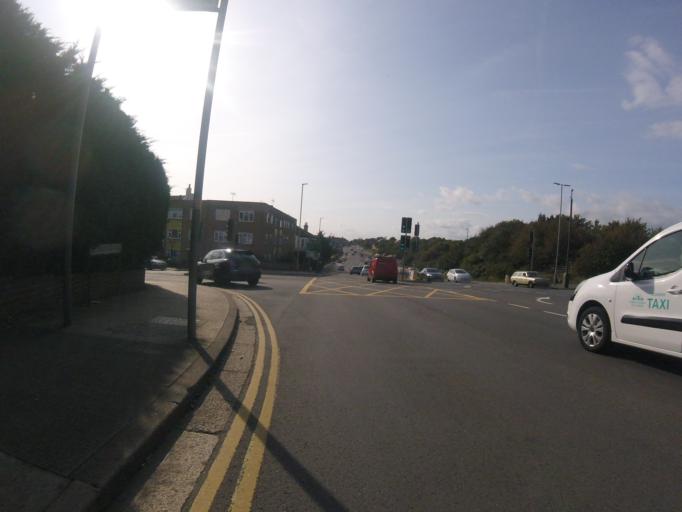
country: GB
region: England
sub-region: East Sussex
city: Portslade
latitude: 50.8380
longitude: -0.2041
